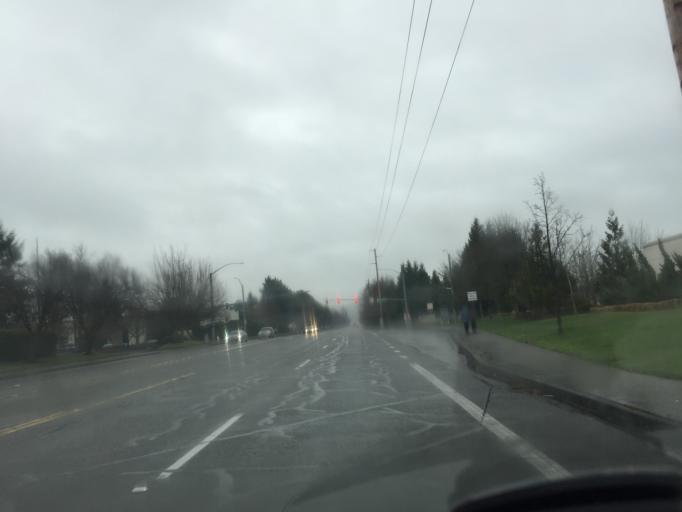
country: US
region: Washington
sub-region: King County
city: SeaTac
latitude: 47.4267
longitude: -122.2588
